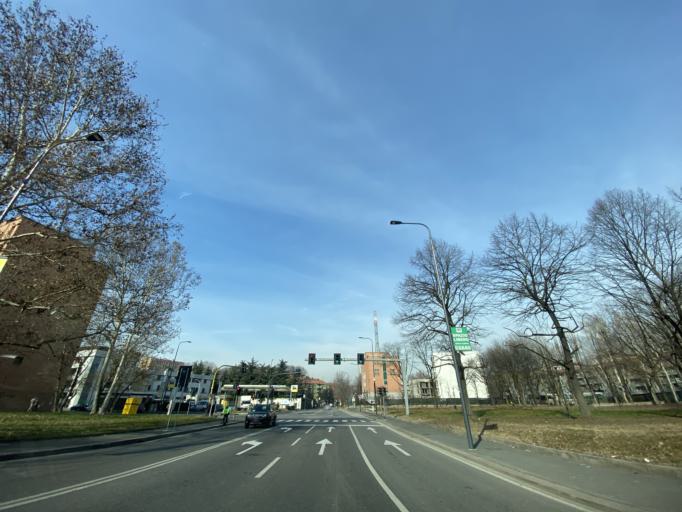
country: IT
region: Lombardy
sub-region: Citta metropolitana di Milano
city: Cormano
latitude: 45.5238
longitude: 9.1667
